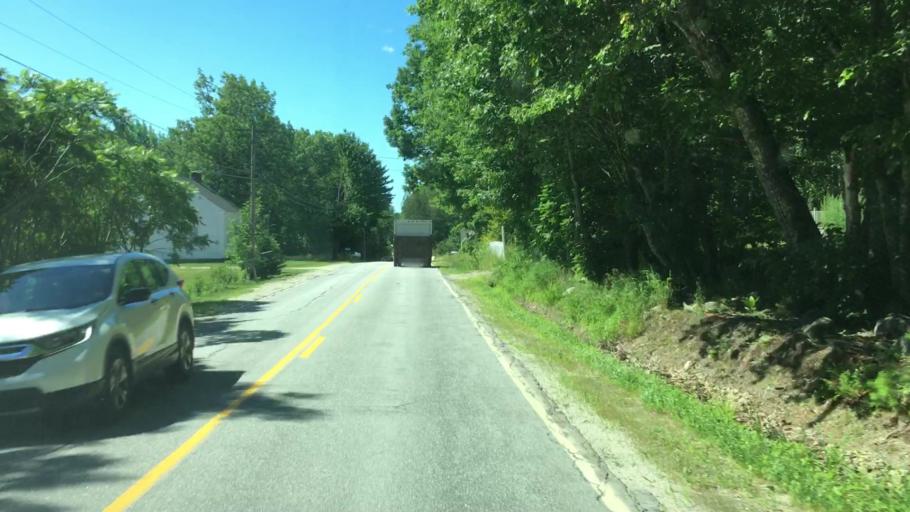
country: US
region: Maine
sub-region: Hancock County
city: Sedgwick
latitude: 44.3439
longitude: -68.5888
